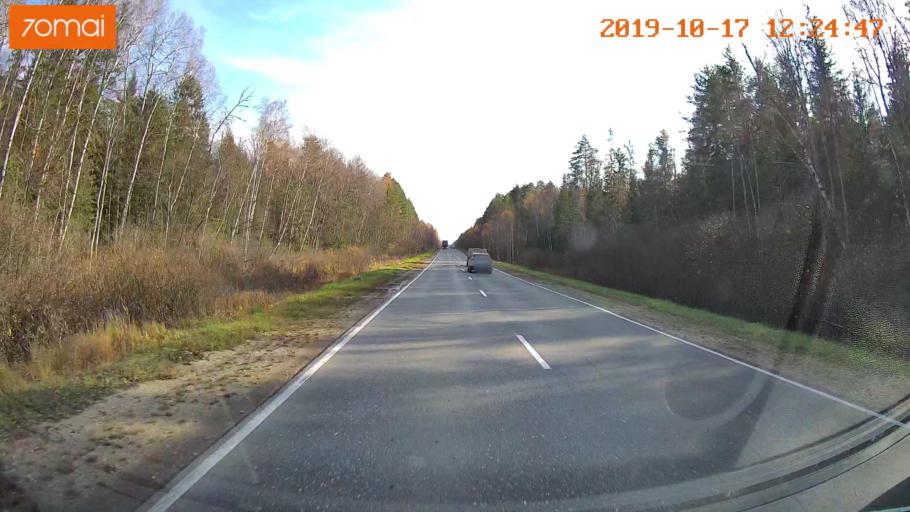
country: RU
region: Rjazan
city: Gus'-Zheleznyy
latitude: 55.0326
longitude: 41.2224
